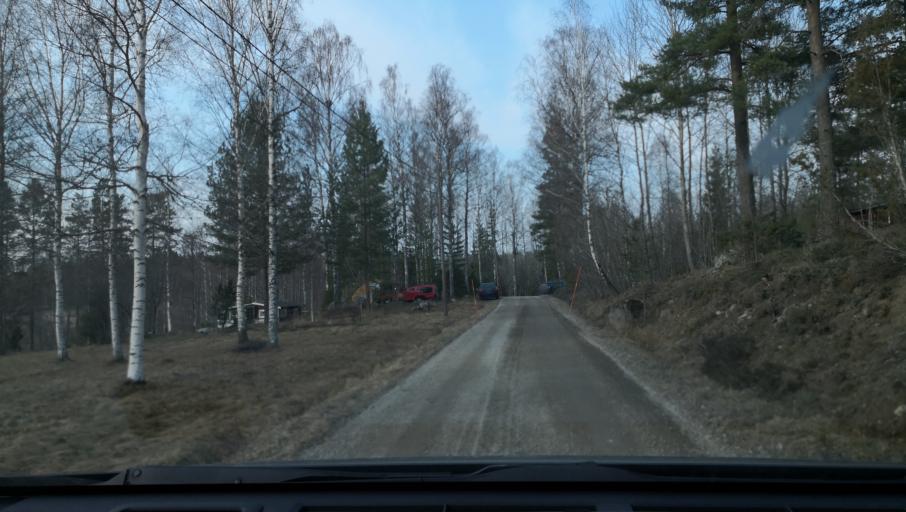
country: SE
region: OErebro
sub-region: Lindesbergs Kommun
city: Frovi
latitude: 59.3838
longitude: 15.3605
